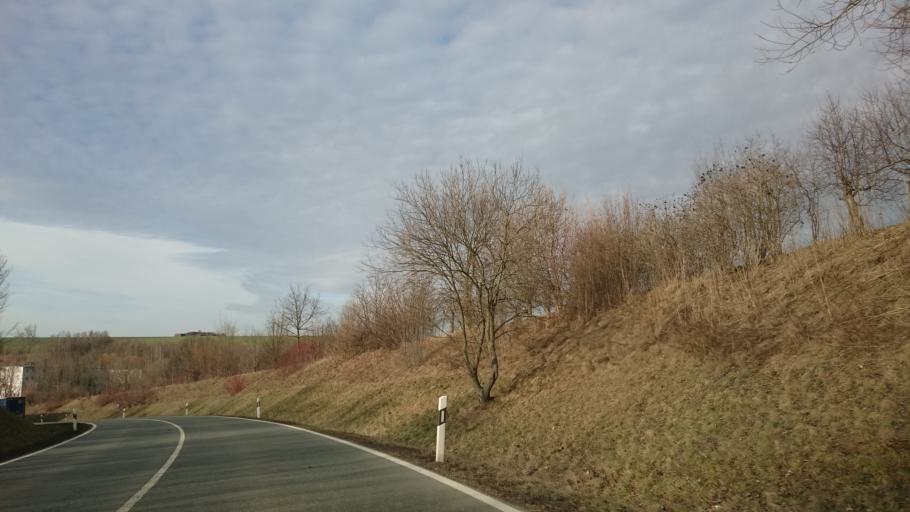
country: DE
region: Saxony
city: Sankt Egidien
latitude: 50.7907
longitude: 12.6293
